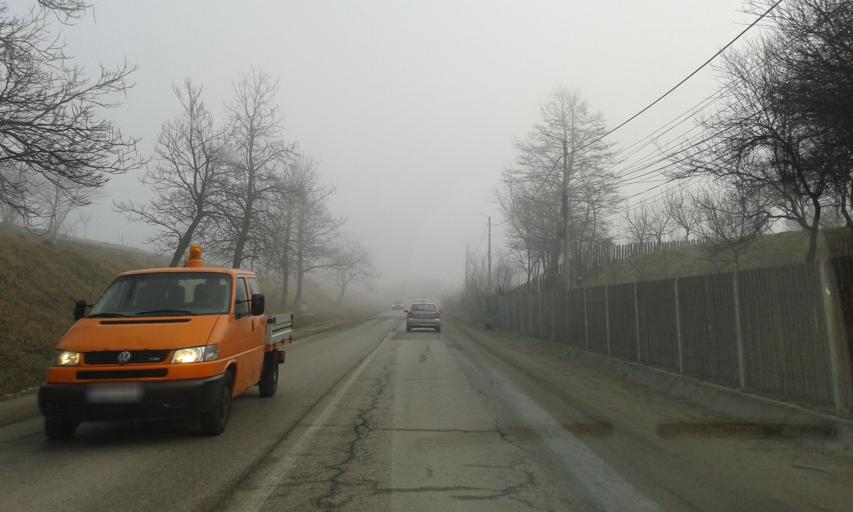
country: RO
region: Hunedoara
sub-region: Municipiul  Vulcan
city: Jiu-Paroseni
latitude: 45.3674
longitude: 23.2711
